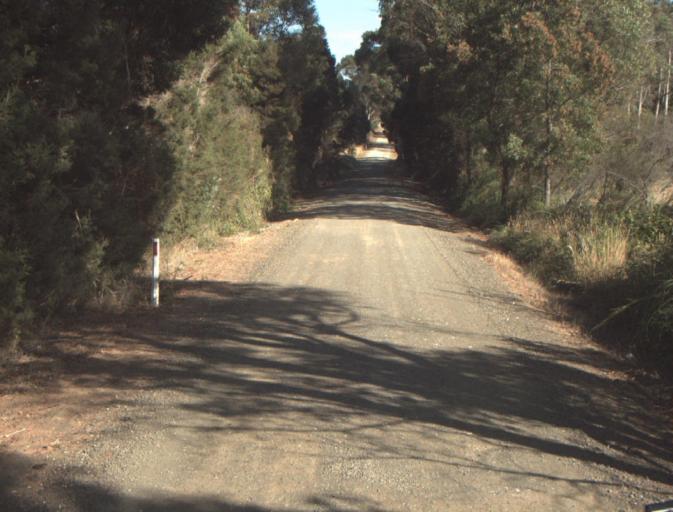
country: AU
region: Tasmania
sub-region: Dorset
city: Bridport
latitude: -41.1558
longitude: 147.2341
